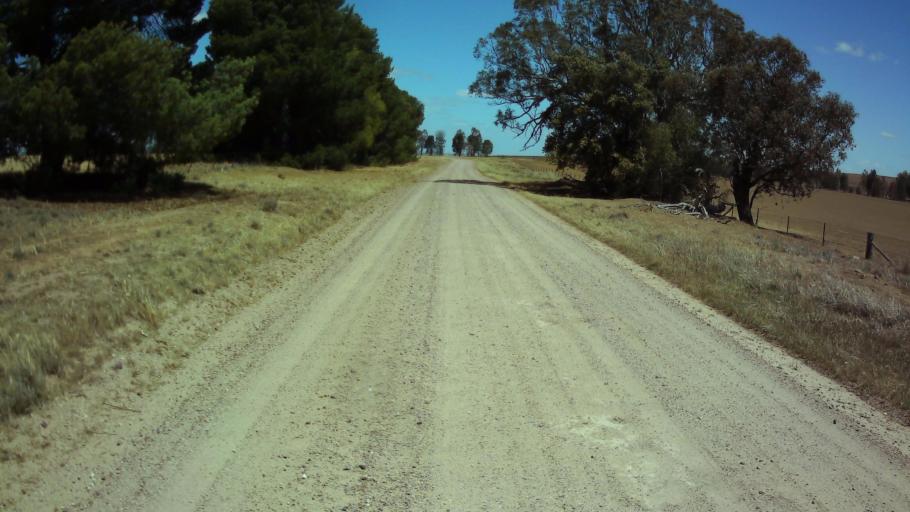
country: AU
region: New South Wales
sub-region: Weddin
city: Grenfell
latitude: -33.9539
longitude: 148.3279
